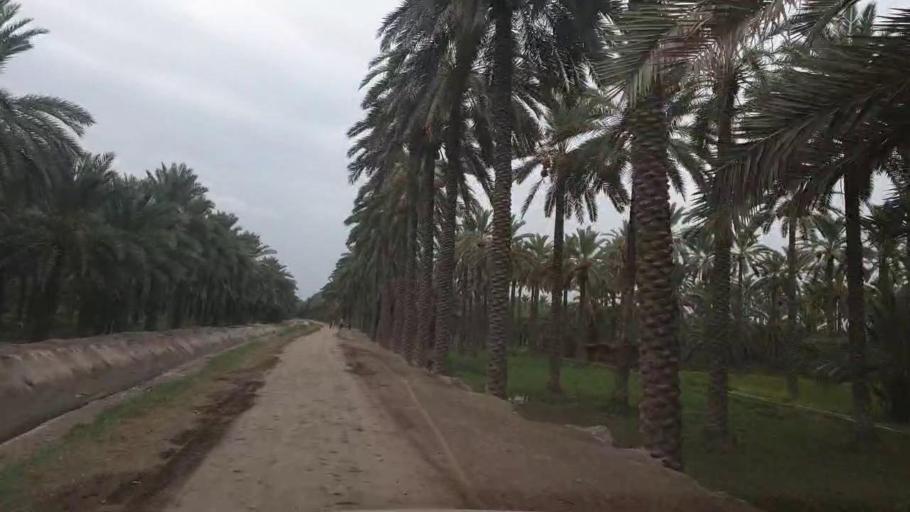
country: PK
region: Sindh
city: Khairpur
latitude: 27.5997
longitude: 68.8013
